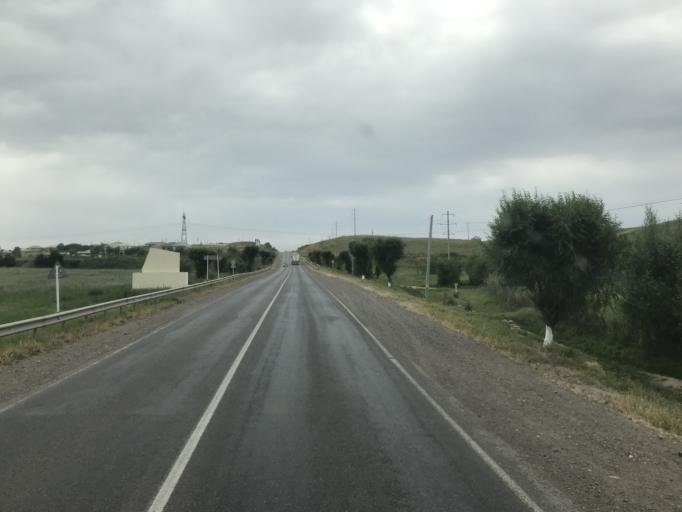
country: KZ
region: Ongtustik Qazaqstan
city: Saryaghash
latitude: 41.4820
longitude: 69.2502
